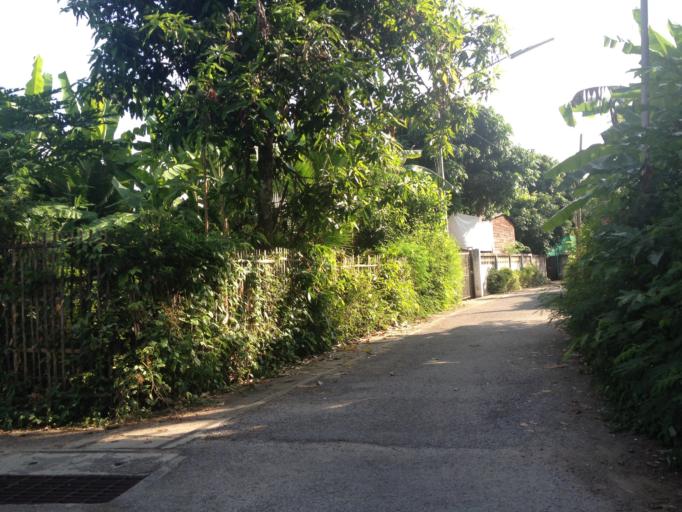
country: TH
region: Chiang Mai
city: Hang Dong
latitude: 18.7031
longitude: 98.9299
